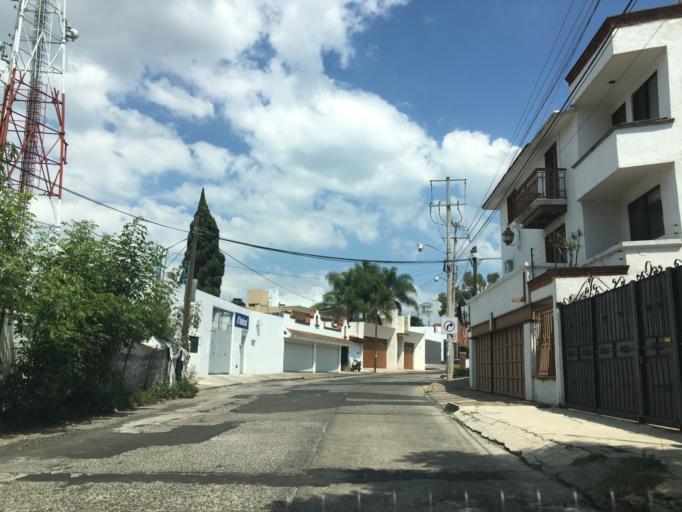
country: MX
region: Michoacan
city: Morelia
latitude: 19.6771
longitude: -101.1854
